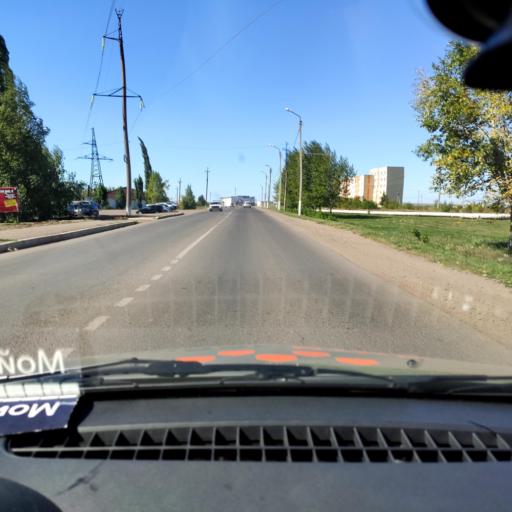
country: RU
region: Bashkortostan
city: Kumertau
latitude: 52.7714
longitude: 55.8019
